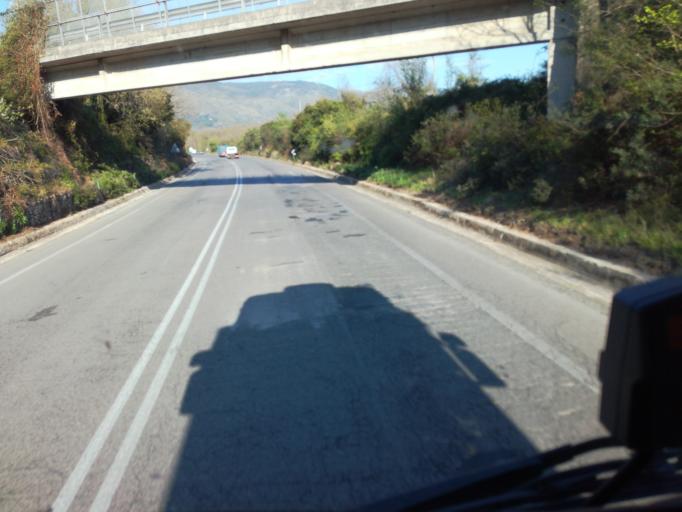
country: IT
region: Latium
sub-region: Provincia di Latina
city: Prossedi
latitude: 41.5093
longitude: 13.2624
